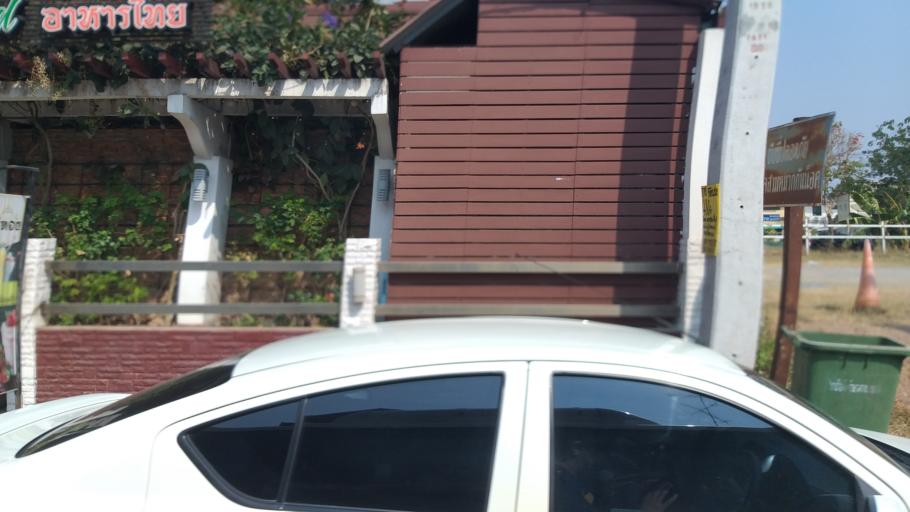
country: TH
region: Changwat Udon Thani
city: Udon Thani
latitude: 17.4192
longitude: 102.7717
